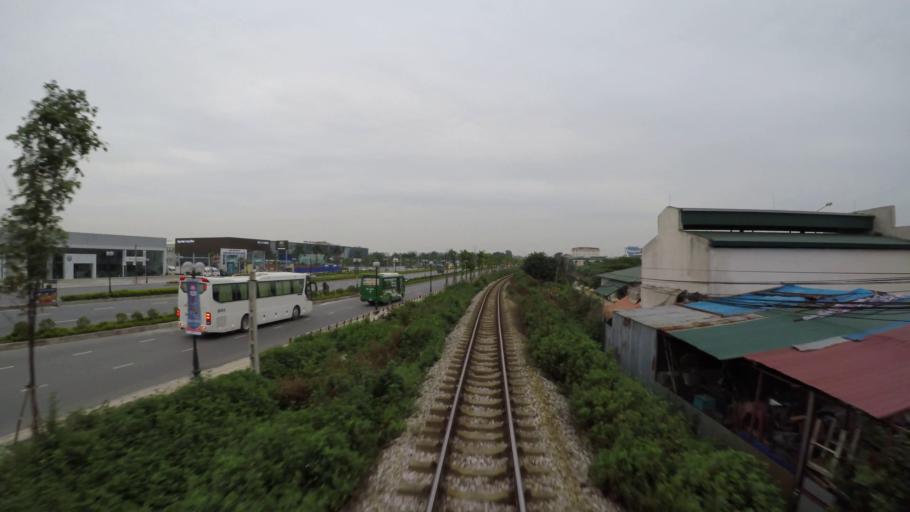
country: VN
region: Ha Noi
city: Trau Quy
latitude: 21.0163
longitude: 105.9448
